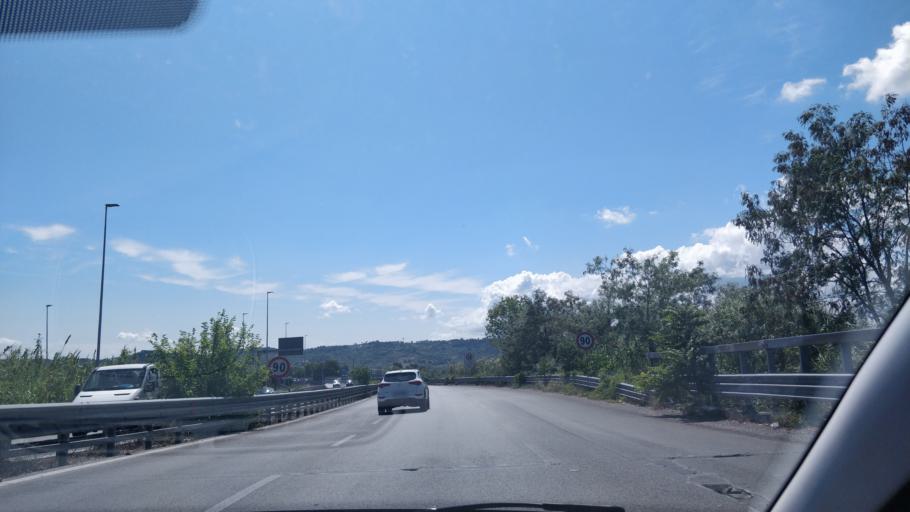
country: IT
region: Abruzzo
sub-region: Provincia di Pescara
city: Villa Raspa
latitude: 42.4506
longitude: 14.1812
